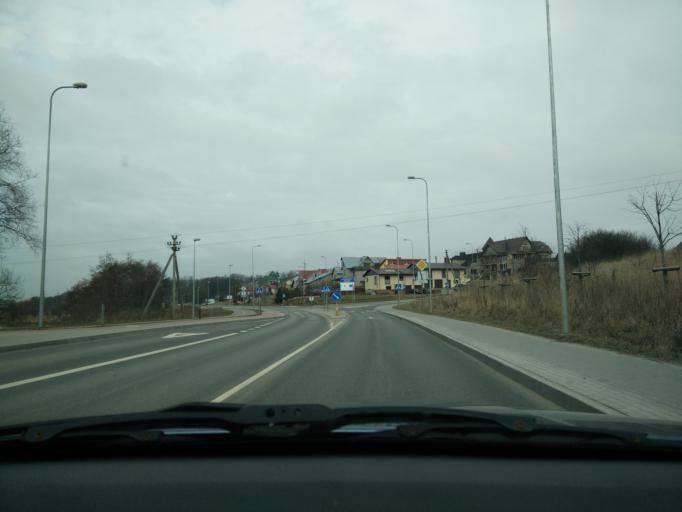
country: LT
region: Klaipedos apskritis
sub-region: Klaipeda
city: Klaipeda
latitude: 55.7174
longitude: 21.1683
